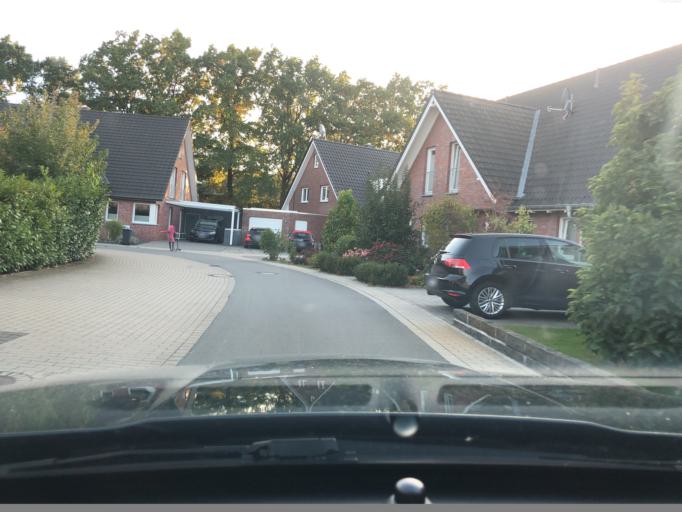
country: DE
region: North Rhine-Westphalia
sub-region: Regierungsbezirk Munster
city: Telgte
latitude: 51.9969
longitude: 7.7134
